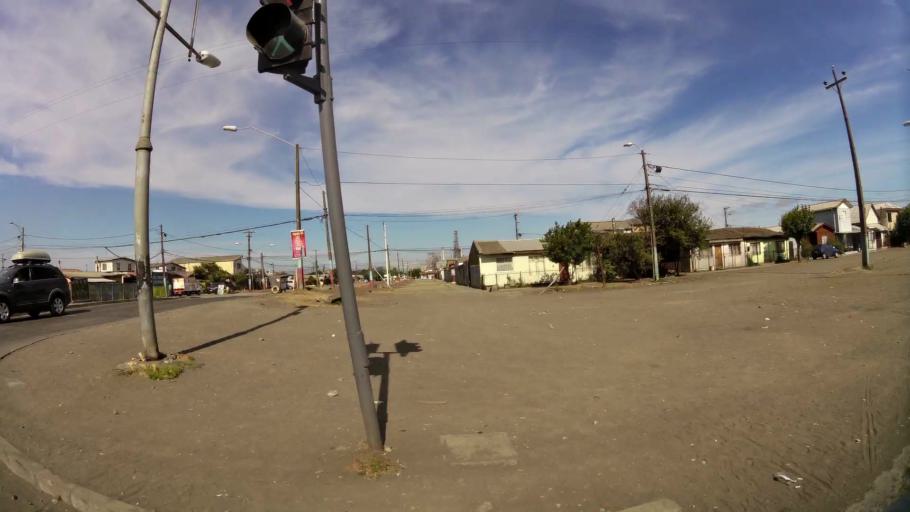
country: CL
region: Biobio
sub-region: Provincia de Concepcion
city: Talcahuano
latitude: -36.7849
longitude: -73.1105
